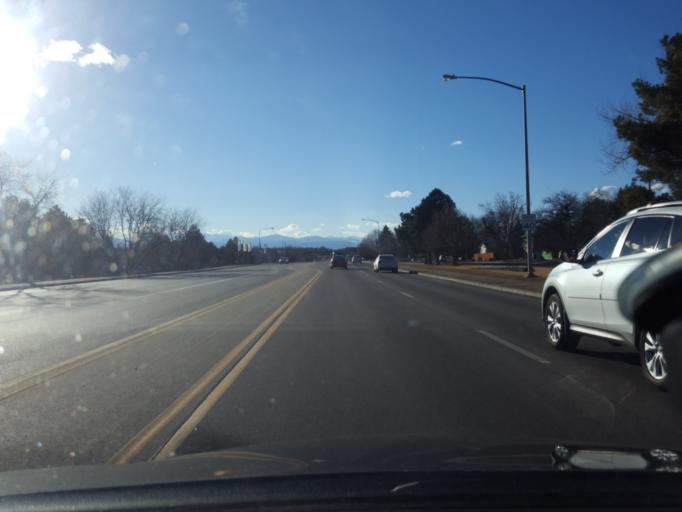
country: US
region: Colorado
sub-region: Adams County
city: Aurora
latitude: 39.7256
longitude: -104.8127
